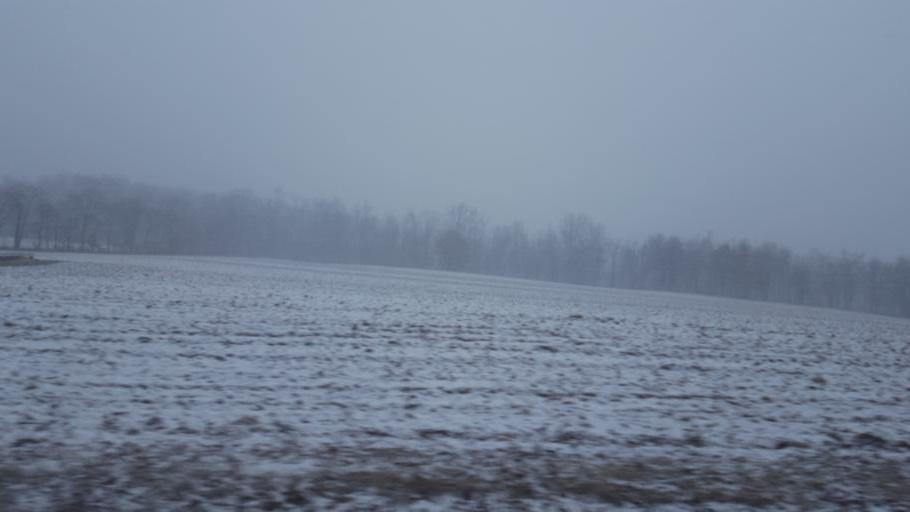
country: US
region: Ohio
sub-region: Coshocton County
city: Coshocton
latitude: 40.3163
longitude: -81.8161
